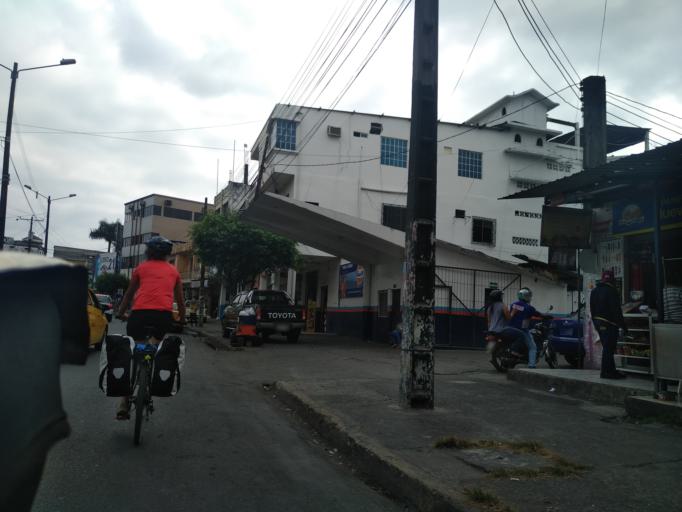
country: EC
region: Los Rios
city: Quevedo
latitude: -1.0311
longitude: -79.4704
